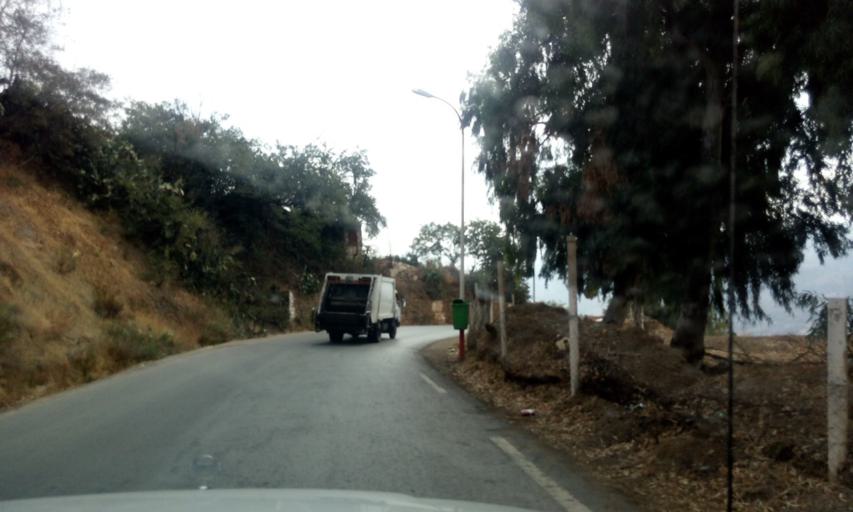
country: DZ
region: Tizi Ouzou
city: Chemini
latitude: 36.6232
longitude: 4.6649
